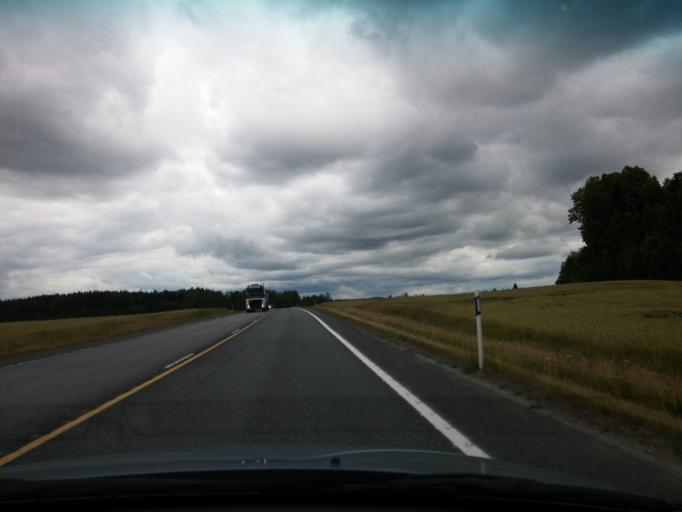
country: FI
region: Uusimaa
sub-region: Porvoo
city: Porvoo
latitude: 60.4001
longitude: 25.5959
